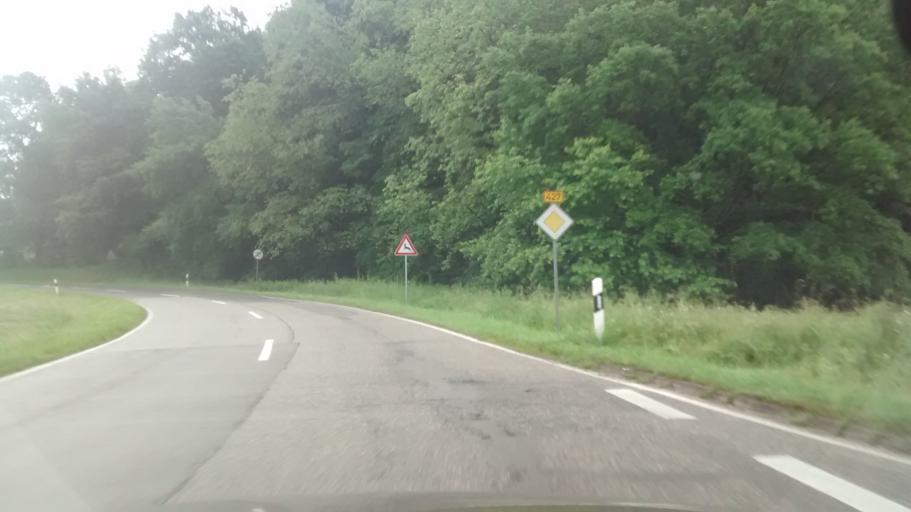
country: DE
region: Rheinland-Pfalz
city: Schindhard
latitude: 49.1373
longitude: 7.8041
